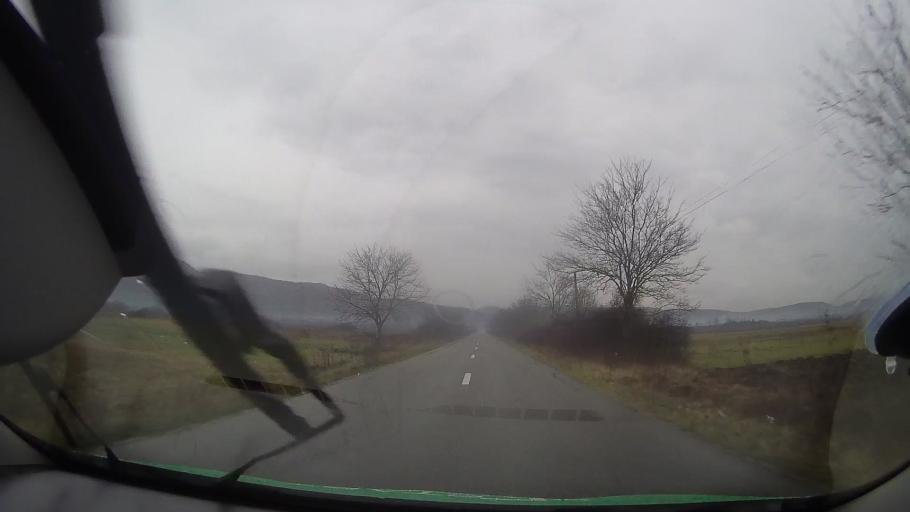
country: RO
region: Bihor
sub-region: Comuna Uileacu de Beius
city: Uileacu de Beius
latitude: 46.6805
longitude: 22.2367
